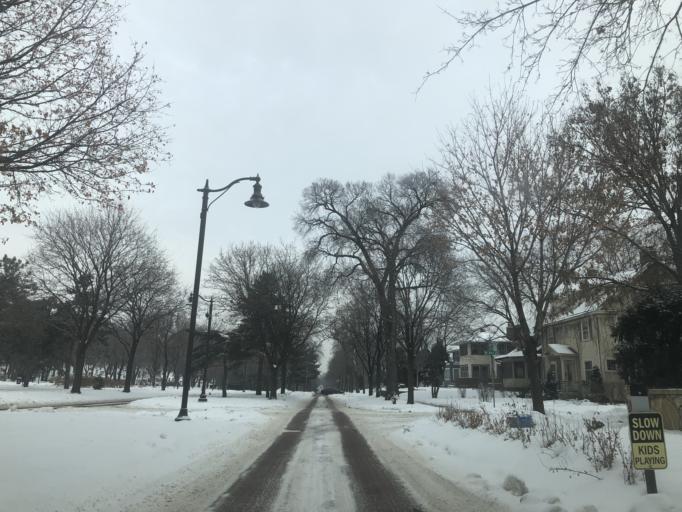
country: US
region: Minnesota
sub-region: Hennepin County
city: Richfield
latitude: 44.9284
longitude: -93.2934
